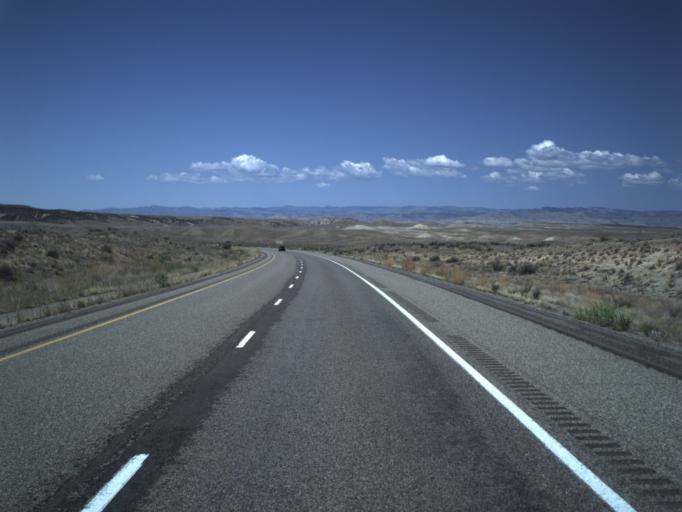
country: US
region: Colorado
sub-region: Mesa County
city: Loma
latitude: 39.1955
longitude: -109.0600
